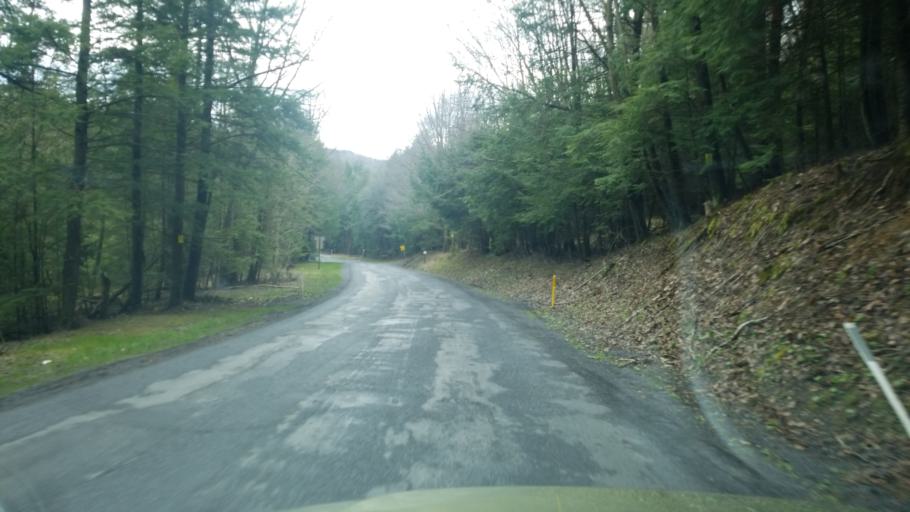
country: US
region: Pennsylvania
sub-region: Clearfield County
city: Clearfield
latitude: 41.0622
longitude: -78.4218
